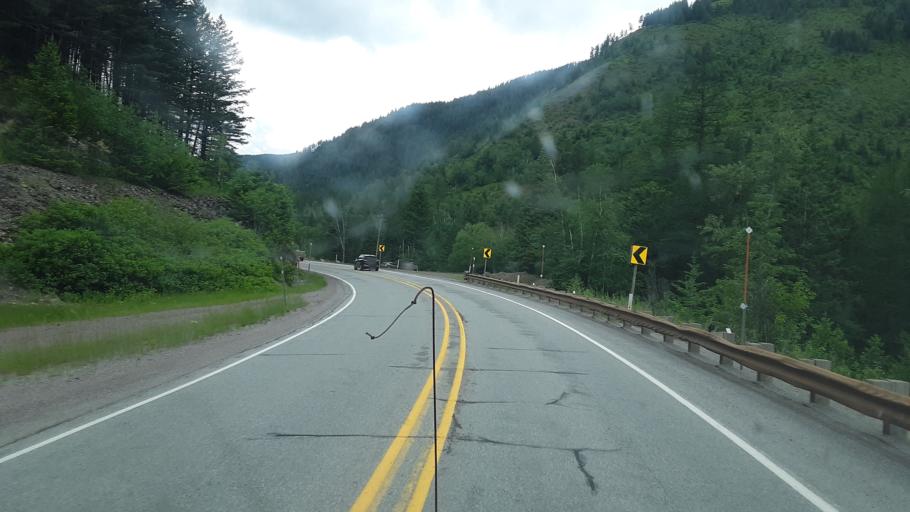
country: US
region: Montana
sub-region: Flathead County
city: Columbia Falls
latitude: 48.4982
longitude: -113.9189
